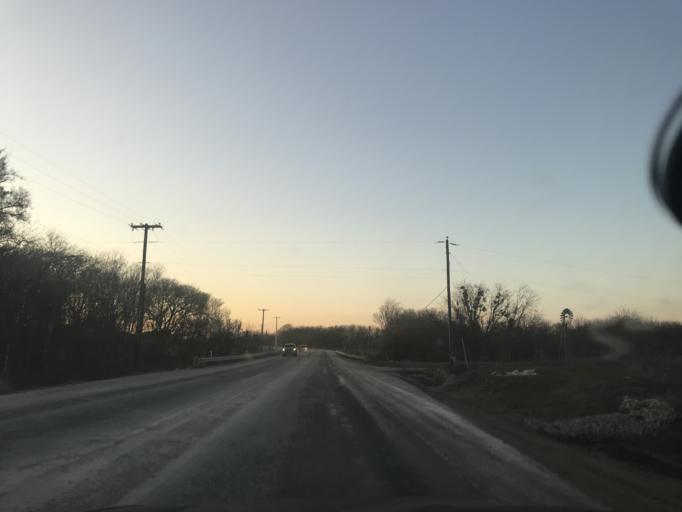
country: US
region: Texas
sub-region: Williamson County
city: Hutto
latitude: 30.5118
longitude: -97.5264
